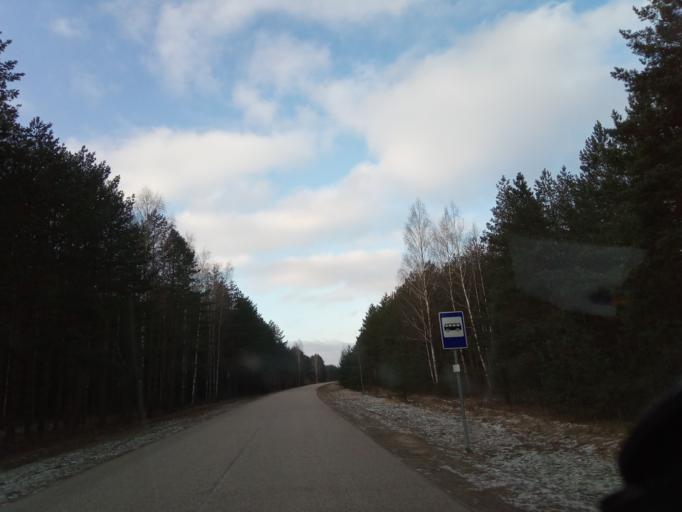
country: LT
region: Alytaus apskritis
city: Druskininkai
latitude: 53.9762
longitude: 24.2494
